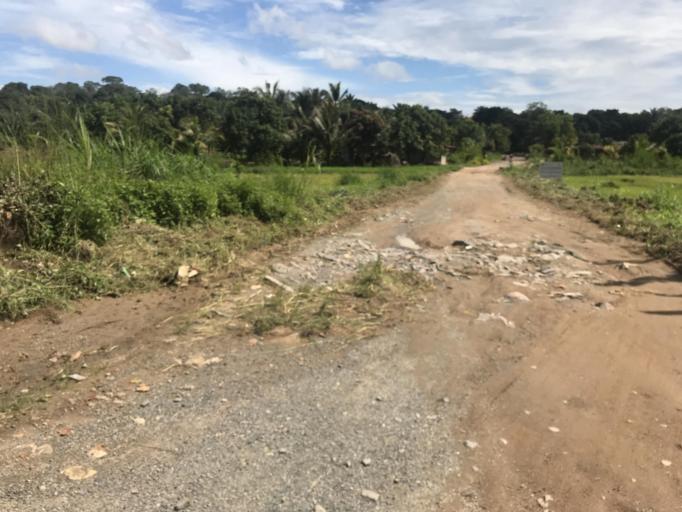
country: SL
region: Eastern Province
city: Koidu
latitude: 8.6437
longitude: -10.9875
